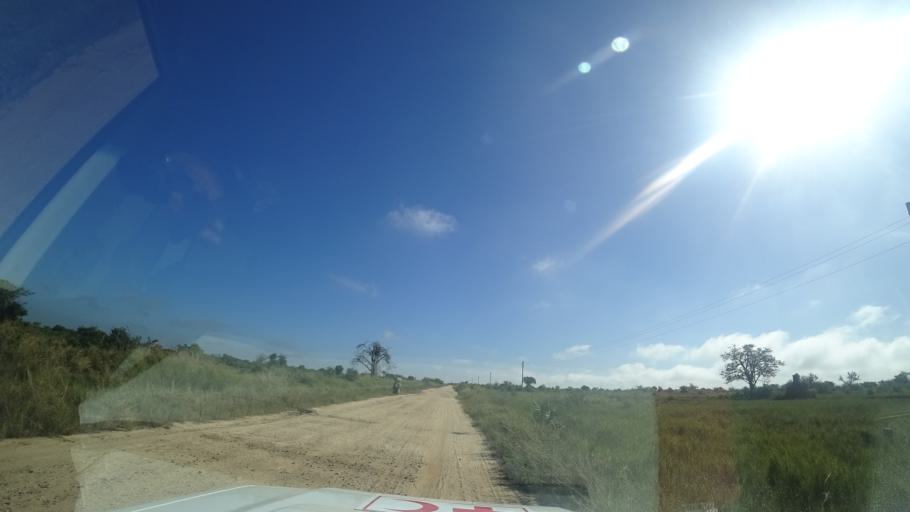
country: MZ
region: Sofala
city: Dondo
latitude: -19.4347
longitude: 34.5612
